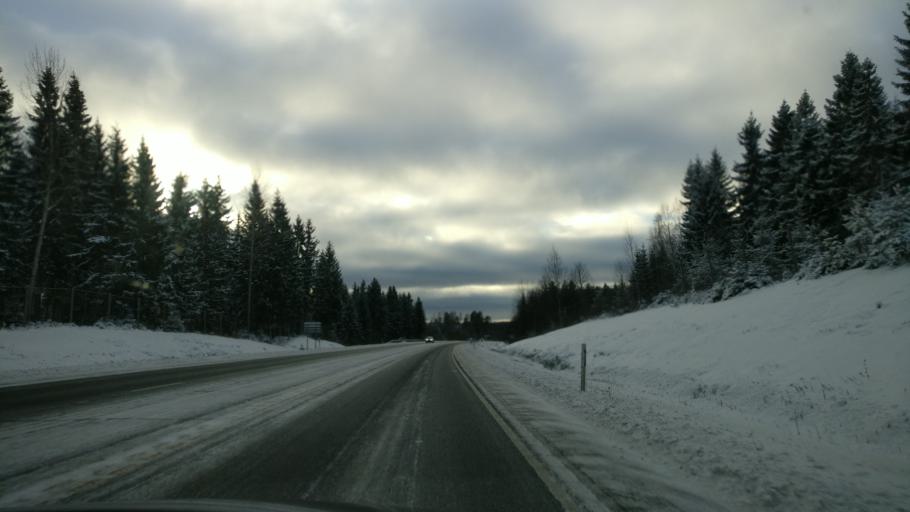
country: FI
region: Southern Savonia
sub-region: Mikkeli
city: Pertunmaa
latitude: 61.3745
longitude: 26.2968
